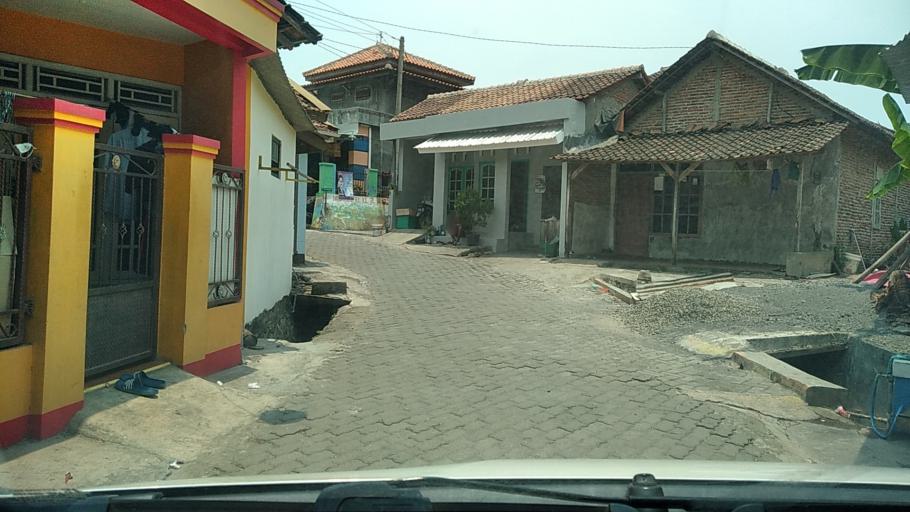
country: ID
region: Central Java
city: Semarang
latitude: -7.0165
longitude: 110.3563
